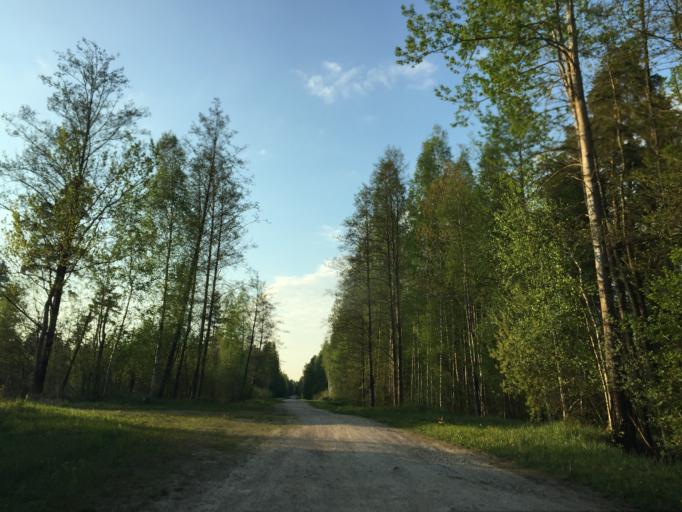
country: LV
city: Tireli
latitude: 56.8830
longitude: 23.6908
